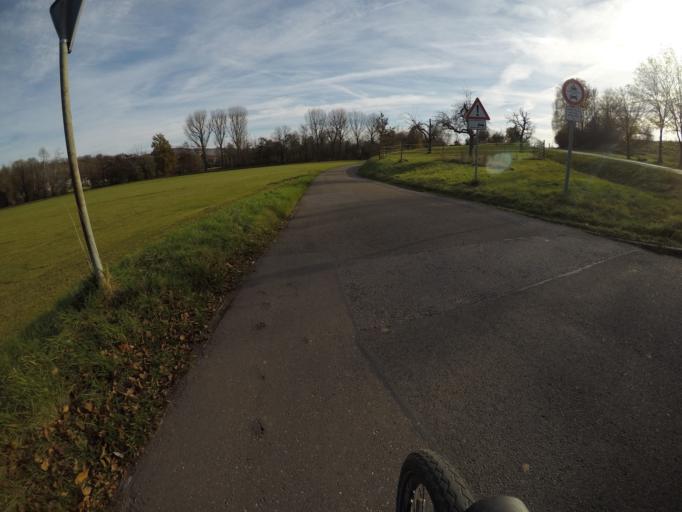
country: DE
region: Baden-Wuerttemberg
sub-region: Regierungsbezirk Stuttgart
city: Waiblingen
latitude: 48.8203
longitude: 9.3346
